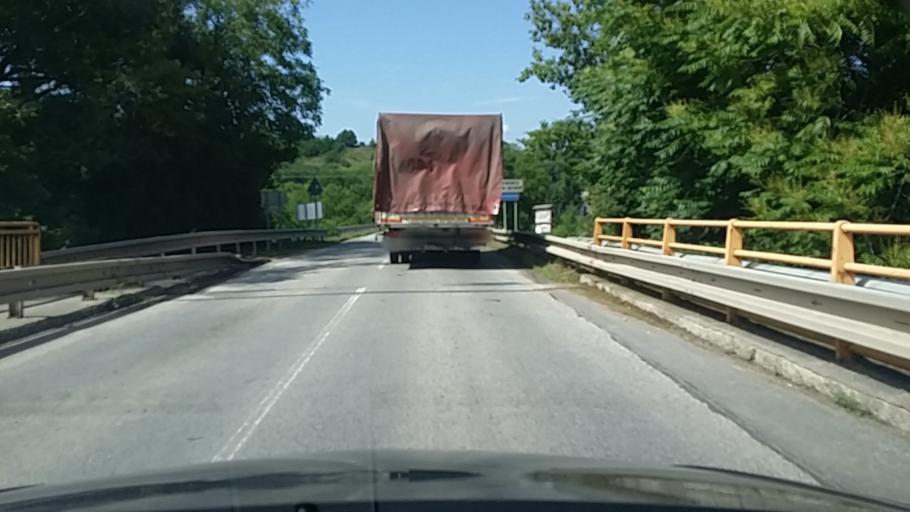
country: SK
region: Nitriansky
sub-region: Okres Nove Zamky
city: Sturovo
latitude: 47.8278
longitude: 18.7201
